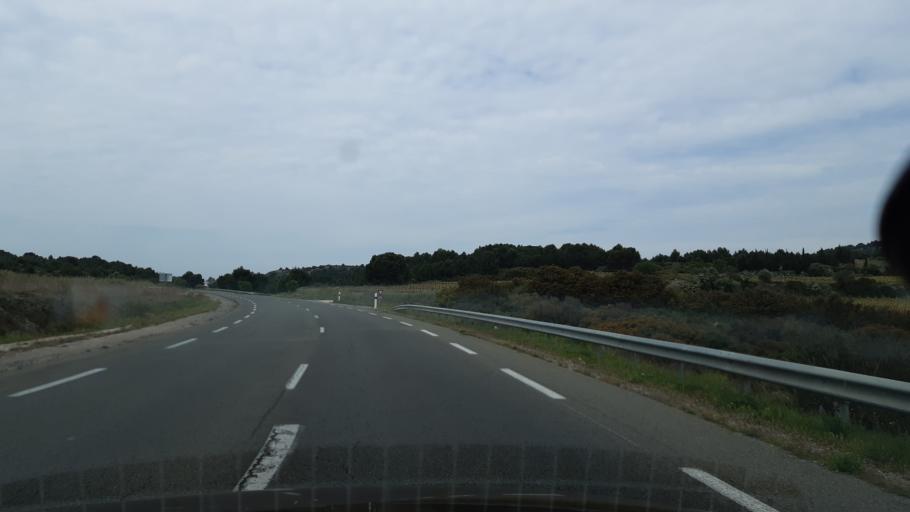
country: FR
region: Languedoc-Roussillon
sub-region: Departement de l'Aude
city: Gruissan
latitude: 43.1227
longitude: 3.0742
